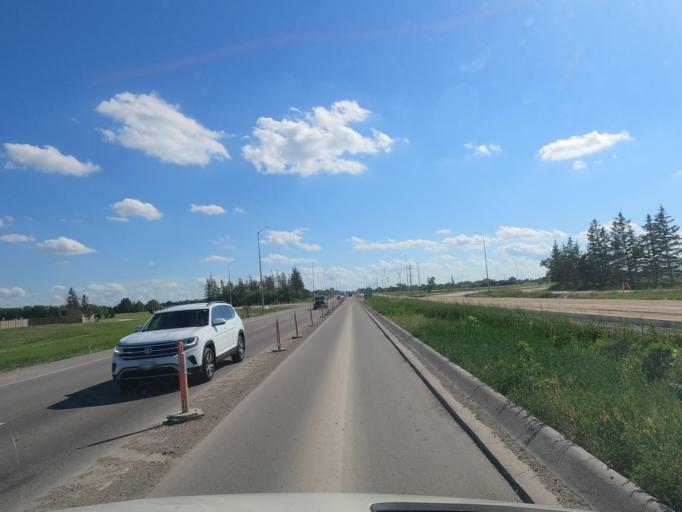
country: CA
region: Manitoba
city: Winnipeg
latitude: 49.9754
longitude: -97.0710
